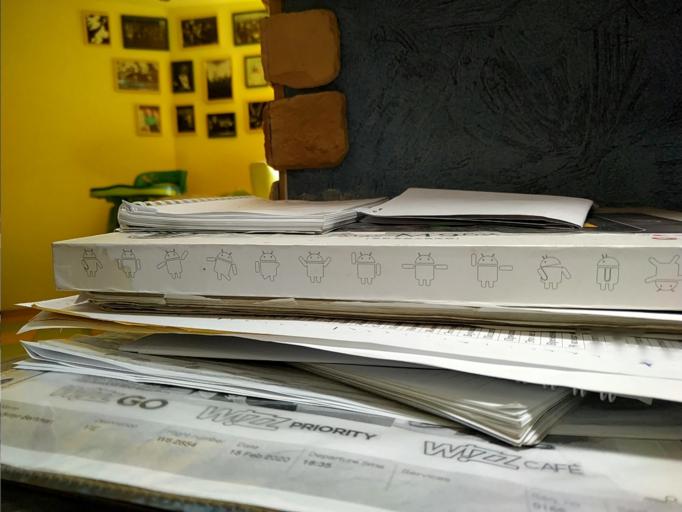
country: RU
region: Novgorod
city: Sol'tsy
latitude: 58.1133
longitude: 30.0922
